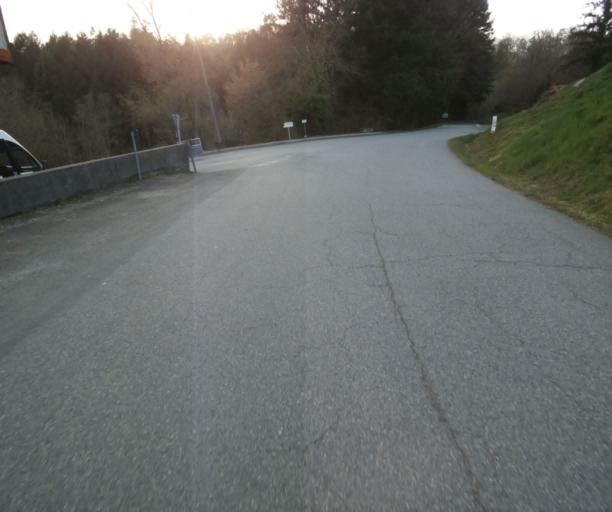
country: FR
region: Limousin
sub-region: Departement de la Correze
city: Correze
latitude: 45.3681
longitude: 1.8714
